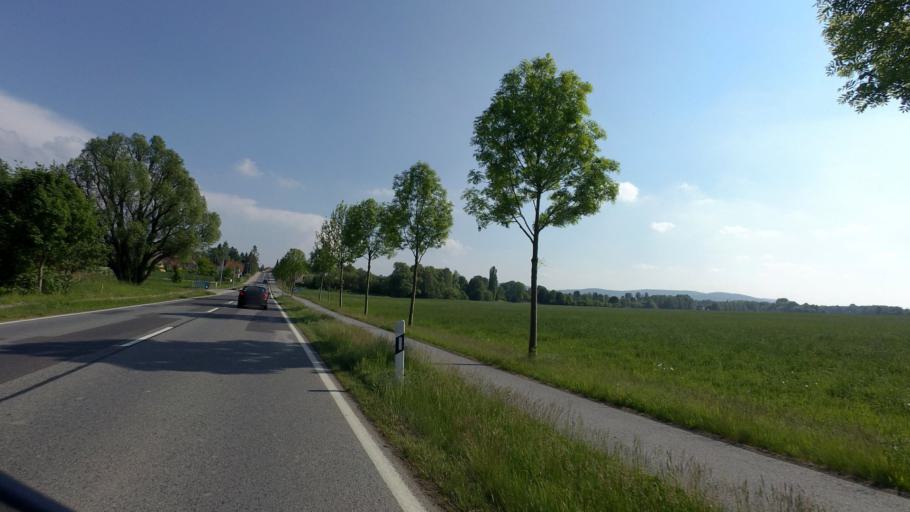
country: DE
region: Saxony
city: Bautzen
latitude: 51.1603
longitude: 14.4299
